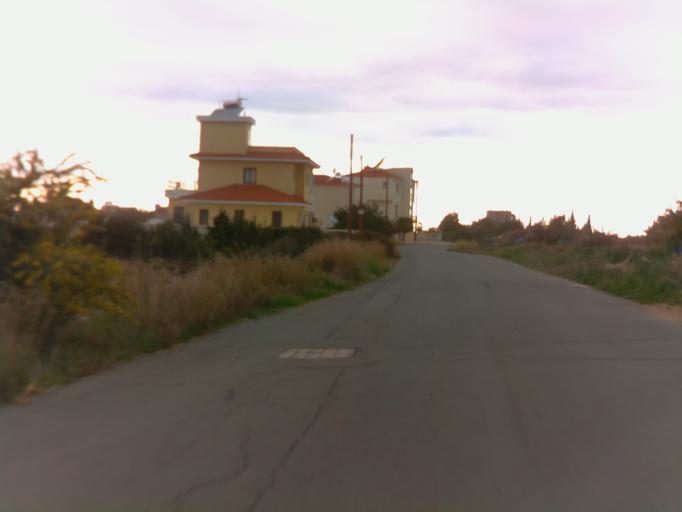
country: CY
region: Pafos
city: Pegeia
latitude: 34.8850
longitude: 32.3399
